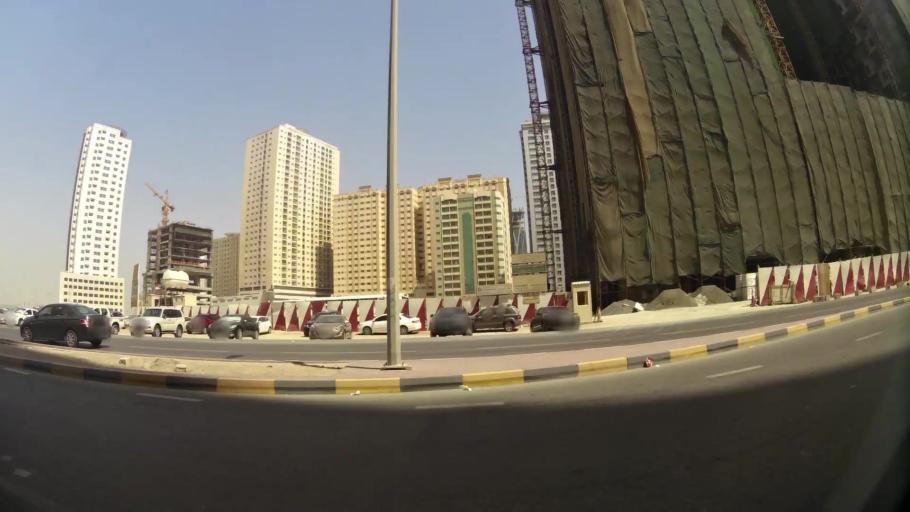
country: AE
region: Ash Shariqah
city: Sharjah
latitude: 25.2998
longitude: 55.3694
